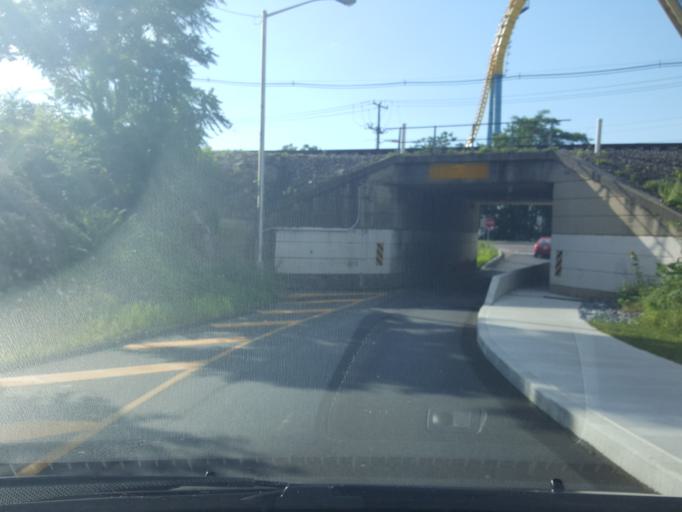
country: US
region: Pennsylvania
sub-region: Dauphin County
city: Hershey
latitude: 40.2849
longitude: -76.6552
